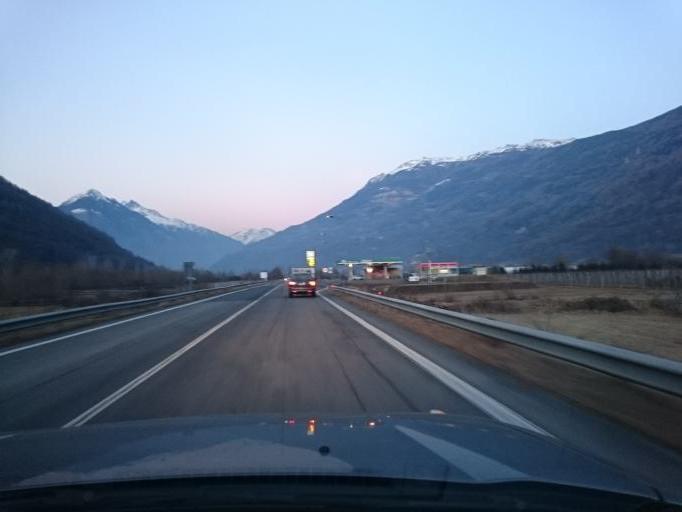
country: IT
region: Lombardy
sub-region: Provincia di Sondrio
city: Lovero
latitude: 46.2369
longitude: 10.2291
